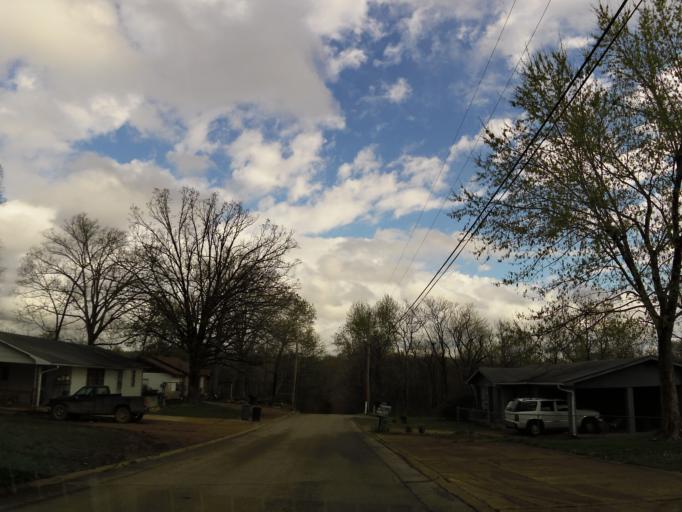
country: US
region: Missouri
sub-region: Butler County
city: Poplar Bluff
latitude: 36.7692
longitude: -90.3884
